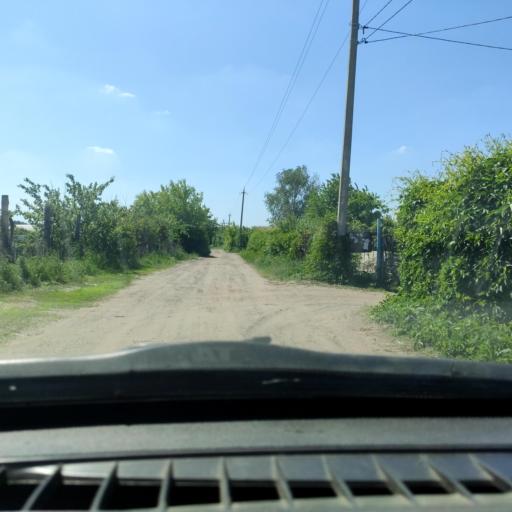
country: RU
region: Samara
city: Povolzhskiy
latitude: 53.5872
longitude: 49.5692
